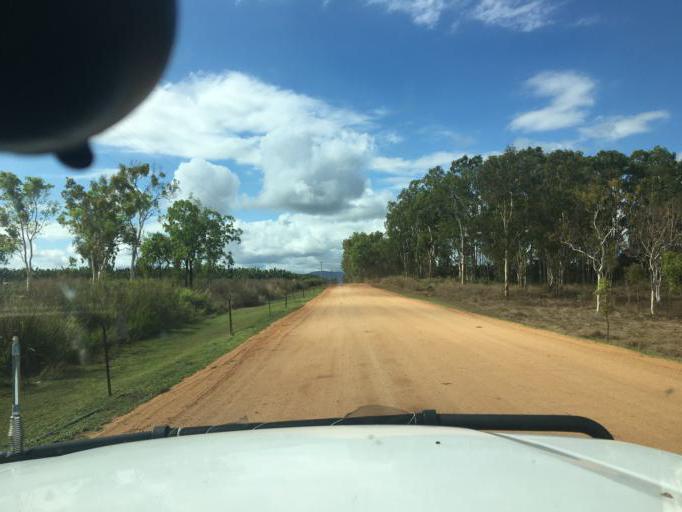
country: AU
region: Queensland
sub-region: Tablelands
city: Mareeba
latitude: -17.0932
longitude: 145.4124
